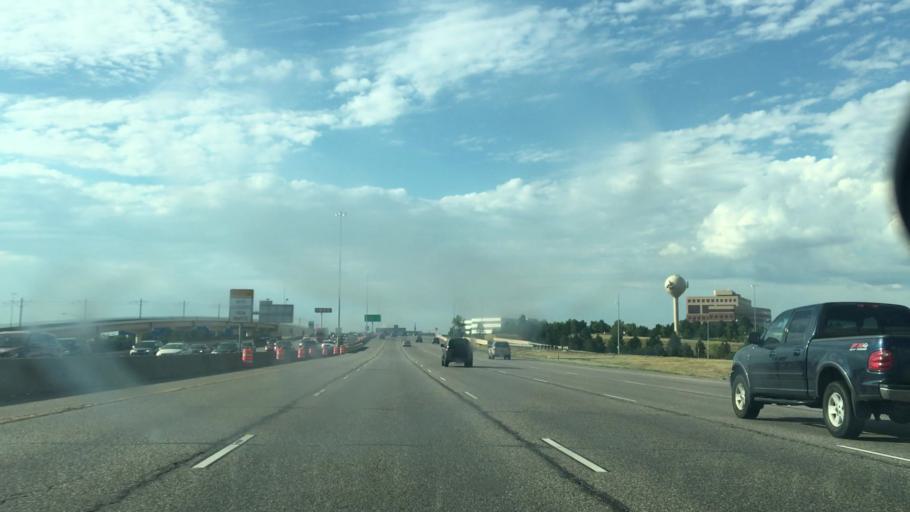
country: US
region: Colorado
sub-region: Arapahoe County
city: Centennial
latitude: 39.5641
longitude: -104.8713
